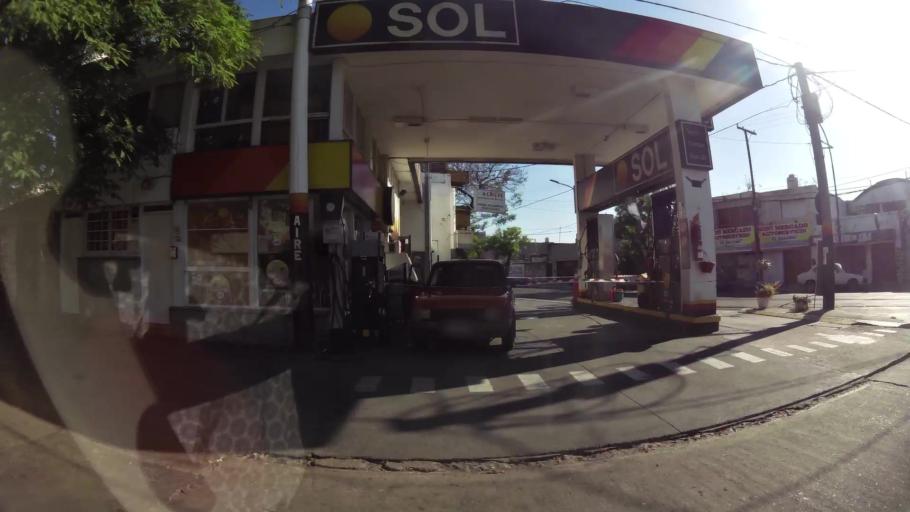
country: AR
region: Cordoba
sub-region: Departamento de Capital
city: Cordoba
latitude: -31.3902
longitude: -64.1758
